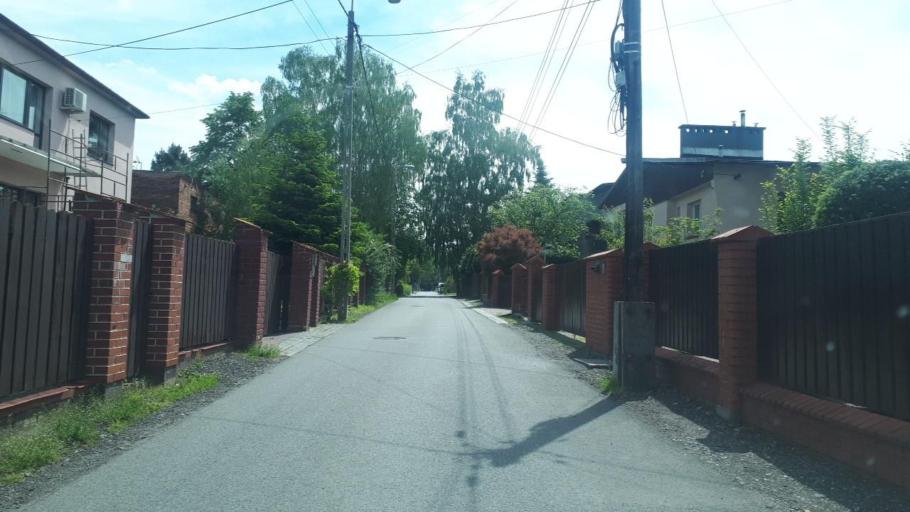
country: PL
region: Silesian Voivodeship
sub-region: Bielsko-Biala
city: Bielsko-Biala
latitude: 49.7966
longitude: 19.0354
